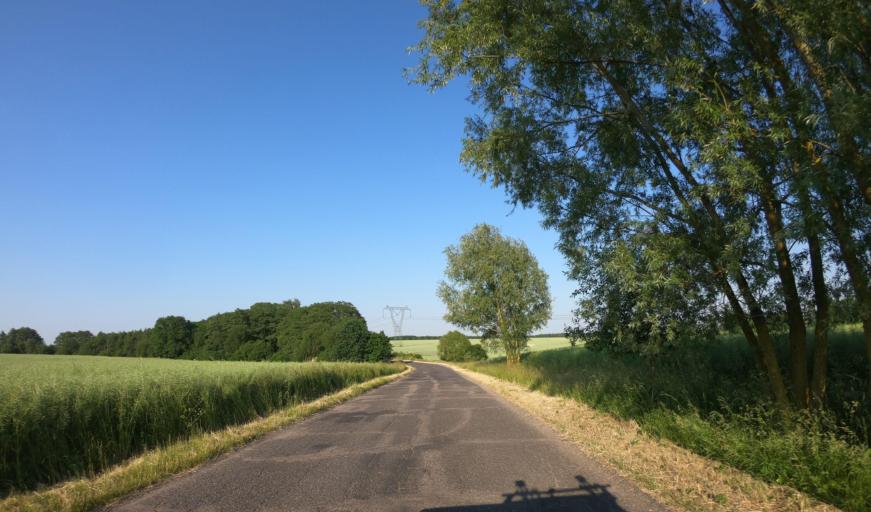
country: PL
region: West Pomeranian Voivodeship
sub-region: Powiat lobeski
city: Radowo Male
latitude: 53.6568
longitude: 15.4190
